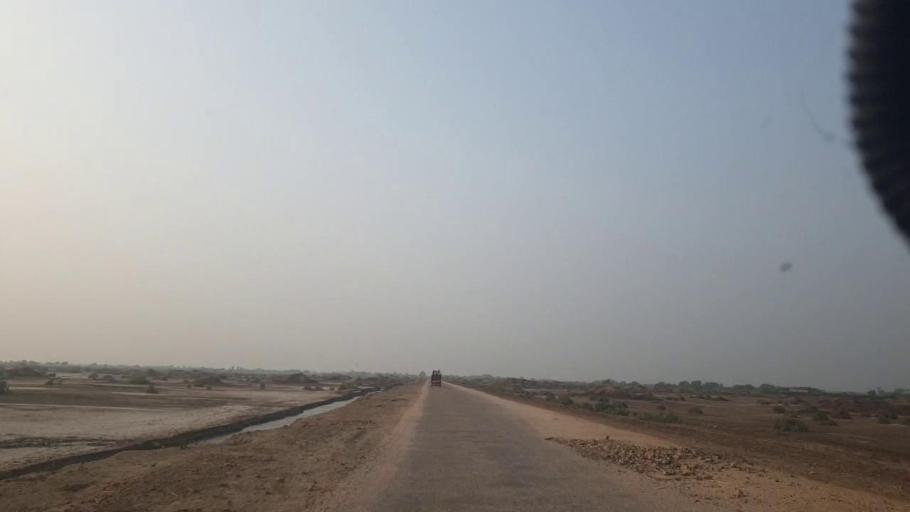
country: PK
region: Sindh
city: Bulri
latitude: 24.8536
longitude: 68.4040
